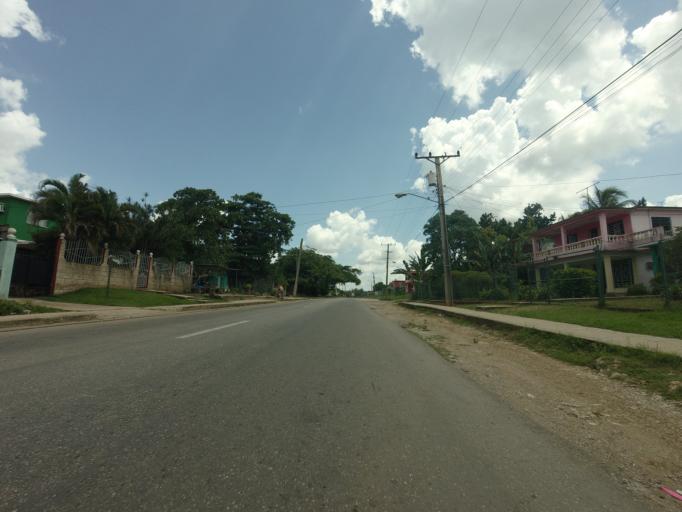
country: CU
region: La Habana
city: Arroyo Naranjo
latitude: 23.0022
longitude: -82.2981
